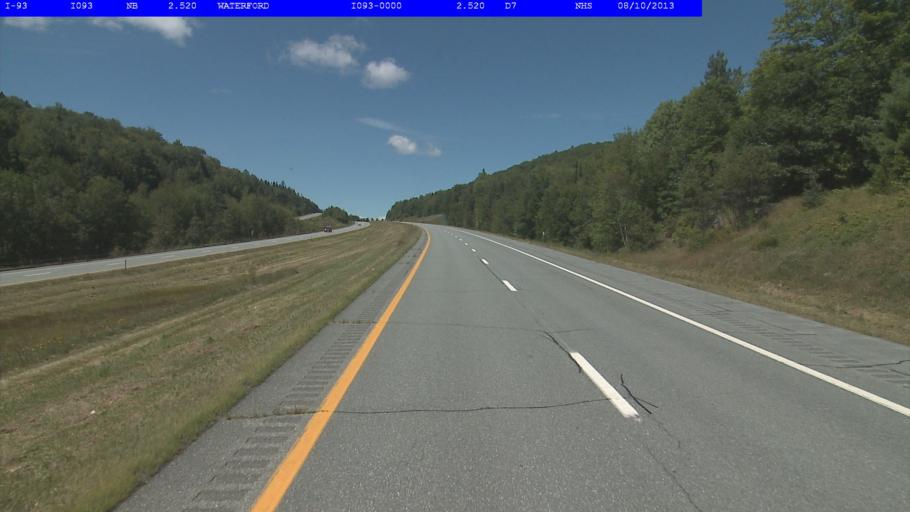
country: US
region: Vermont
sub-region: Caledonia County
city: Saint Johnsbury
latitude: 44.3760
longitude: -71.9114
